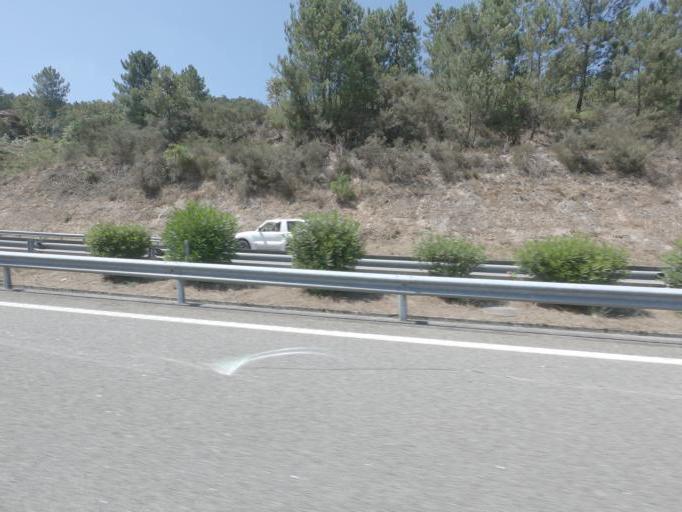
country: PT
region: Porto
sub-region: Amarante
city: Amarante
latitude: 41.2537
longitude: -8.1027
